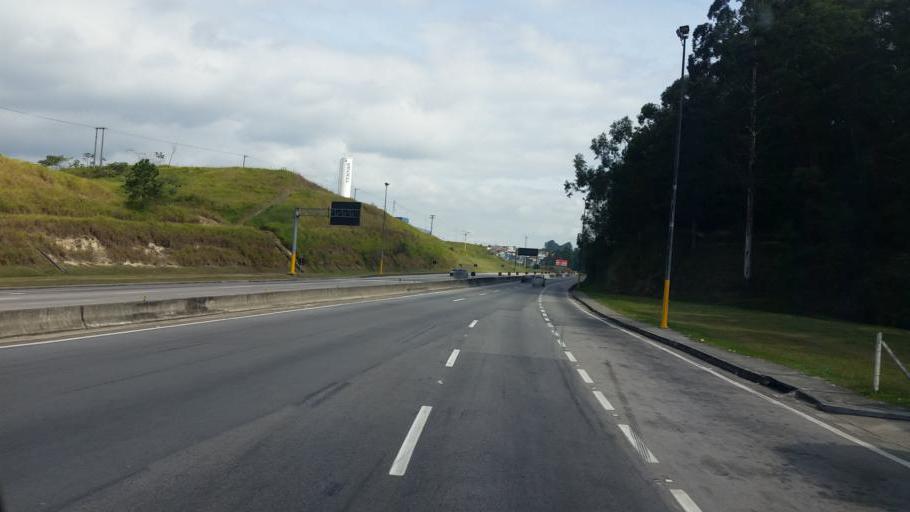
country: BR
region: Sao Paulo
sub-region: Jacarei
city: Jacarei
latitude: -23.2974
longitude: -46.0092
